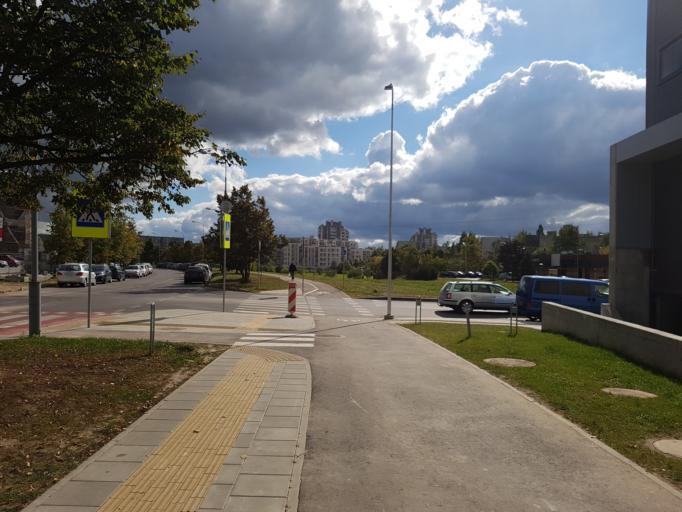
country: LT
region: Vilnius County
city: Seskine
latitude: 54.7210
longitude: 25.2463
